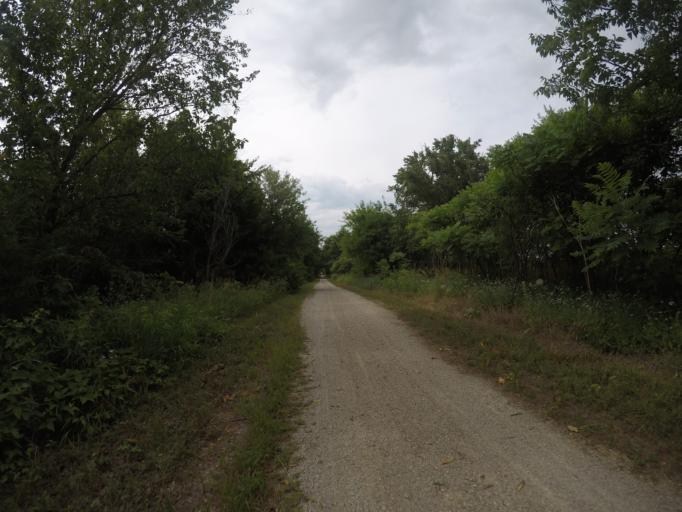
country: US
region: Kansas
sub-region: Franklin County
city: Ottawa
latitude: 38.5037
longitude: -95.2731
